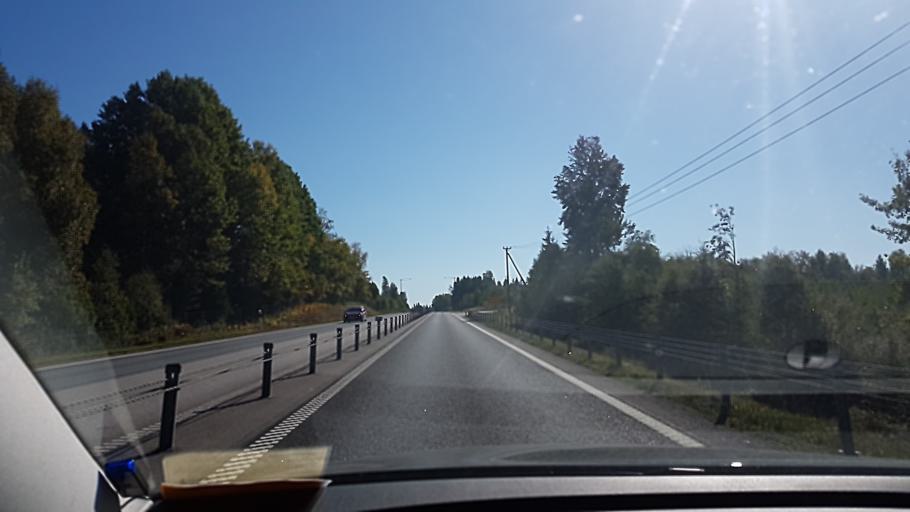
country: SE
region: Kronoberg
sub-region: Vaxjo Kommun
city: Vaexjoe
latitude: 56.8803
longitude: 14.8941
